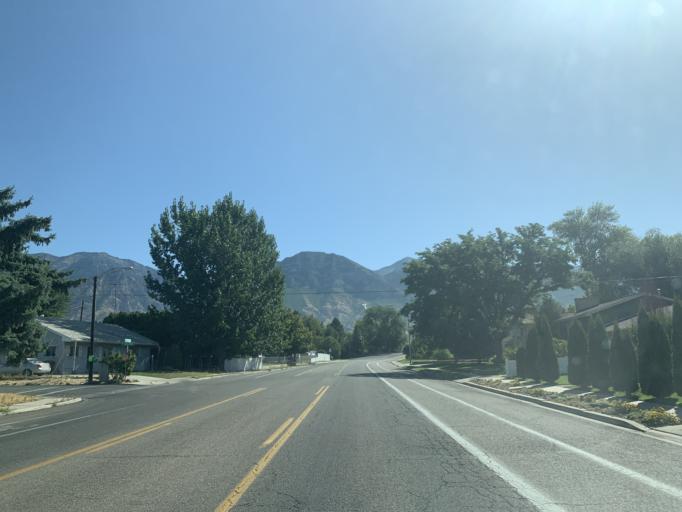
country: US
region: Utah
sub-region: Utah County
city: Provo
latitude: 40.2448
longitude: -111.6765
